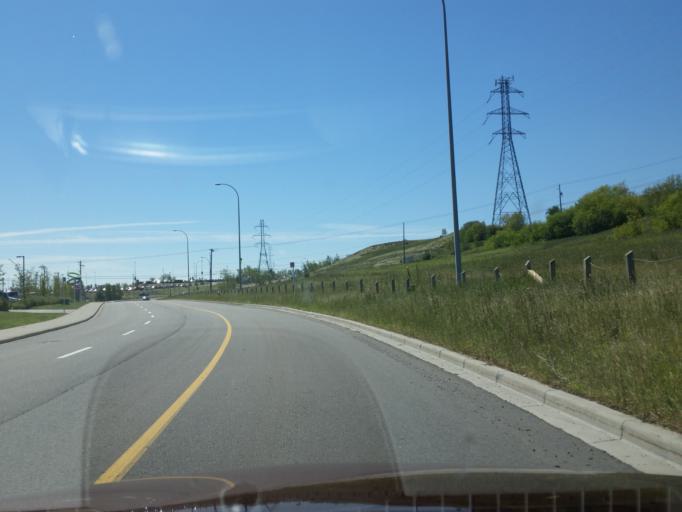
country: CA
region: Alberta
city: Calgary
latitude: 51.0542
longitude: -114.0266
